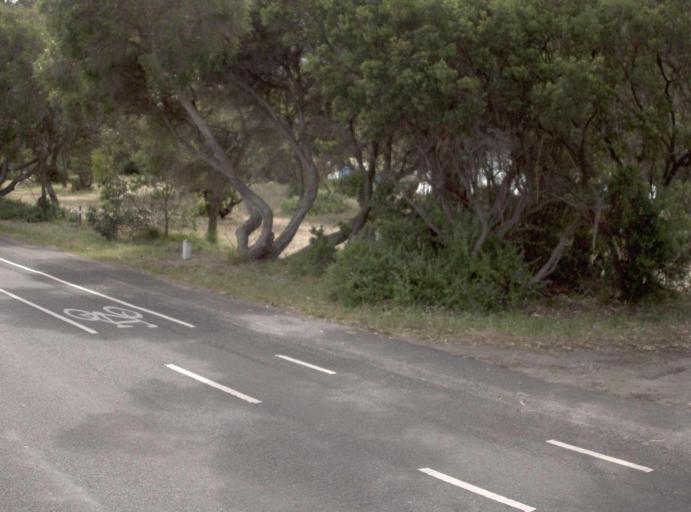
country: AU
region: Victoria
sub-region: Mornington Peninsula
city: Tootgarook
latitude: -38.3686
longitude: 144.8552
